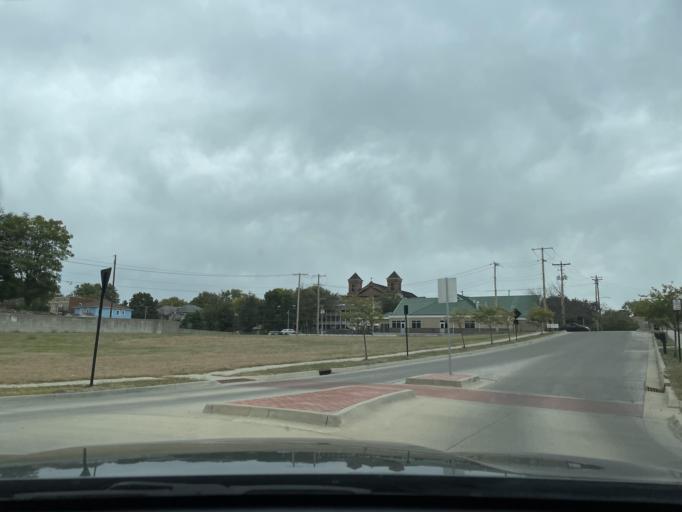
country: US
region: Missouri
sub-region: Buchanan County
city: Saint Joseph
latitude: 39.7698
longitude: -94.8505
